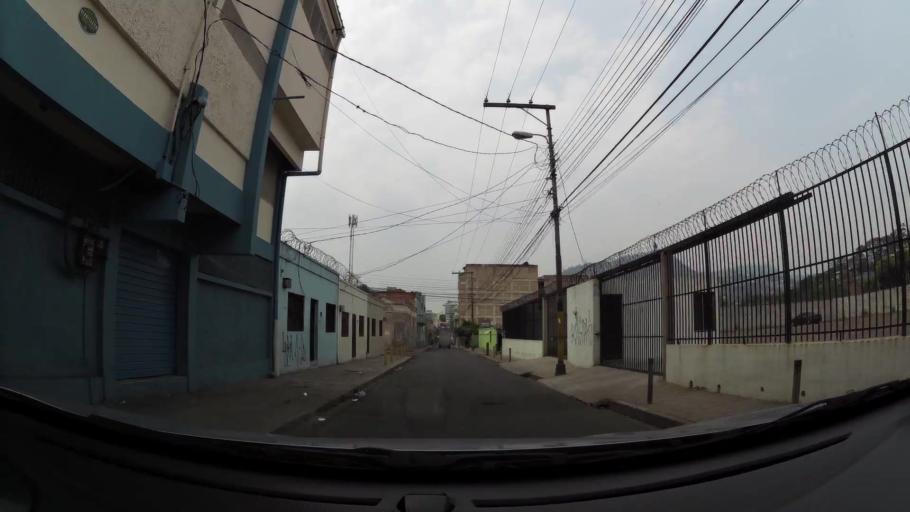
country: HN
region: Francisco Morazan
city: Tegucigalpa
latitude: 14.0991
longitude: -87.2063
